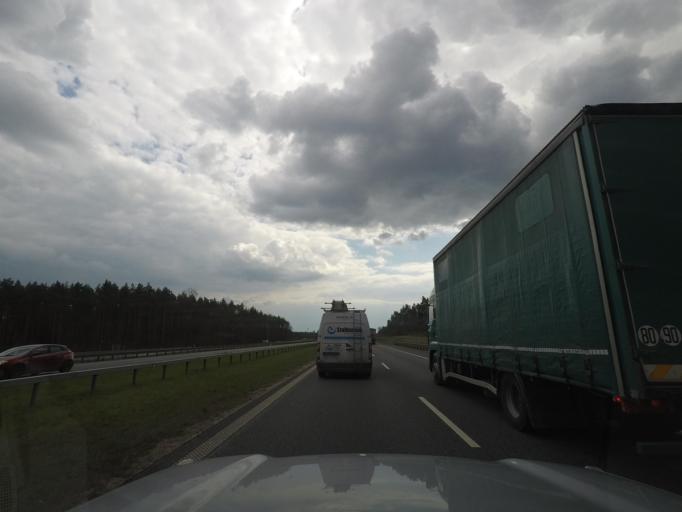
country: PL
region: Lower Silesian Voivodeship
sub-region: Powiat lubinski
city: Osiek
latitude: 51.3202
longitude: 16.1610
